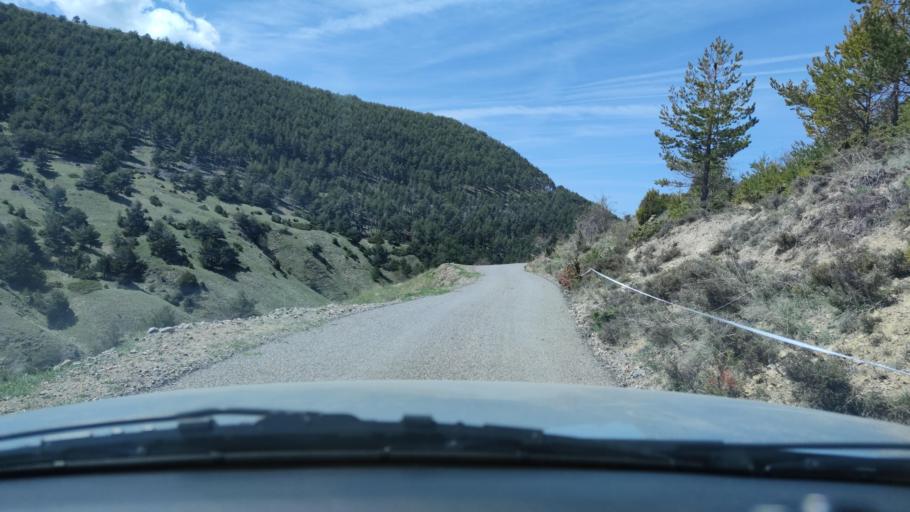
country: ES
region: Catalonia
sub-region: Provincia de Lleida
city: Sort
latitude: 42.3103
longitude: 1.1709
